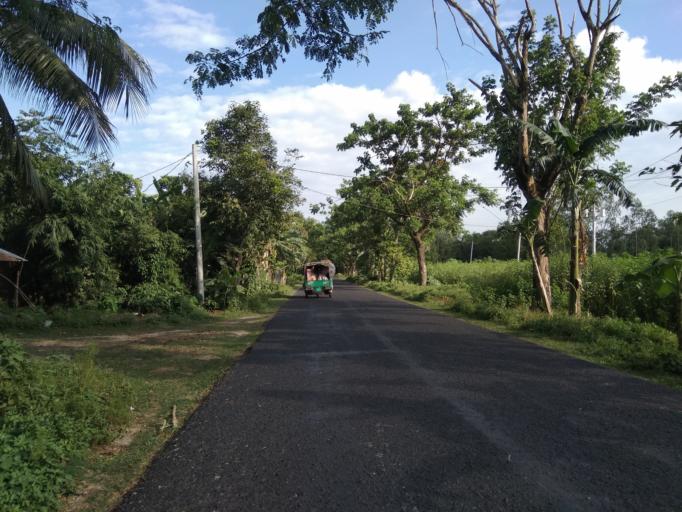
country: BD
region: Rangpur Division
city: Rangpur
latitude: 25.8421
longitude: 89.1130
